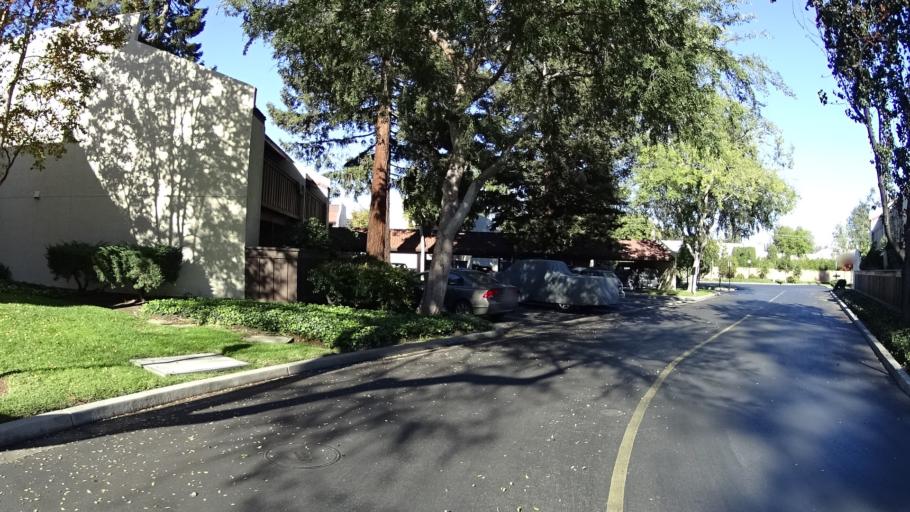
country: US
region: California
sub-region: Santa Clara County
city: Sunnyvale
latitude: 37.3714
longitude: -122.0079
